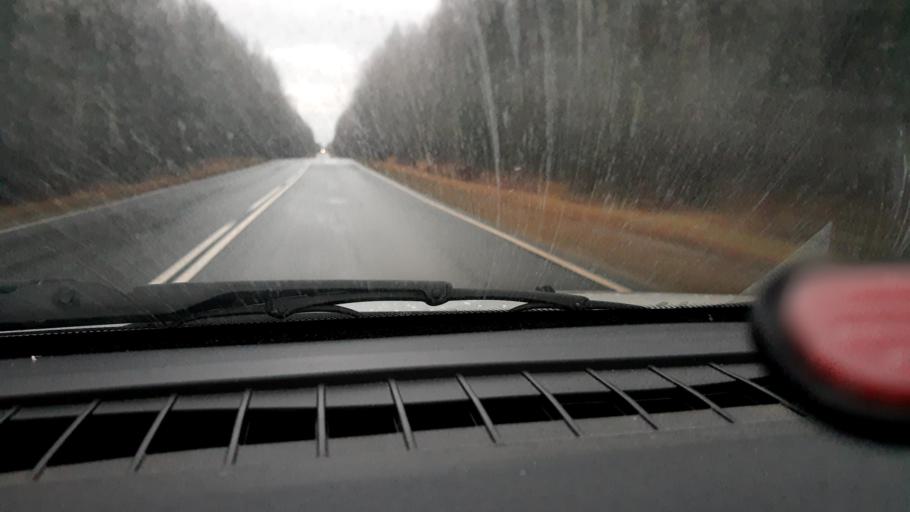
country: RU
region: Nizjnij Novgorod
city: Uren'
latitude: 57.2581
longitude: 45.6123
